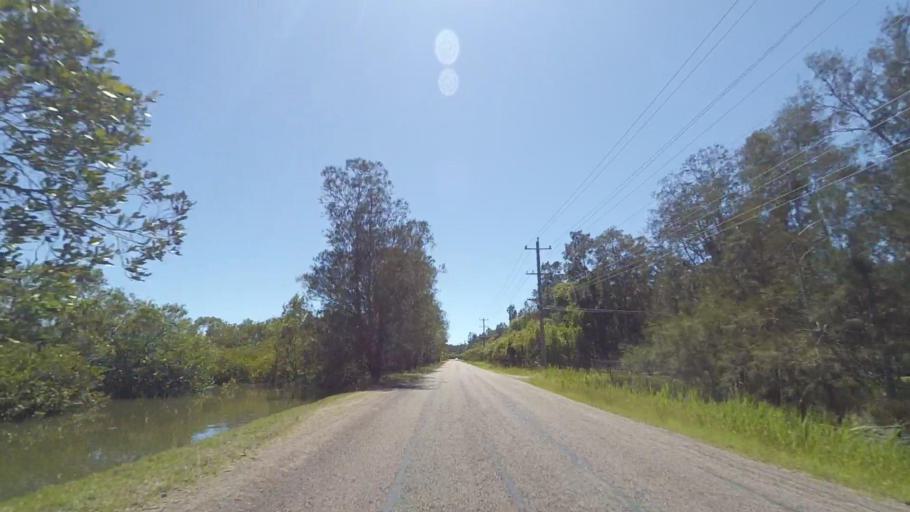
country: AU
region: New South Wales
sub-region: Port Stephens Shire
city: Medowie
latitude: -32.7788
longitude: 151.9630
